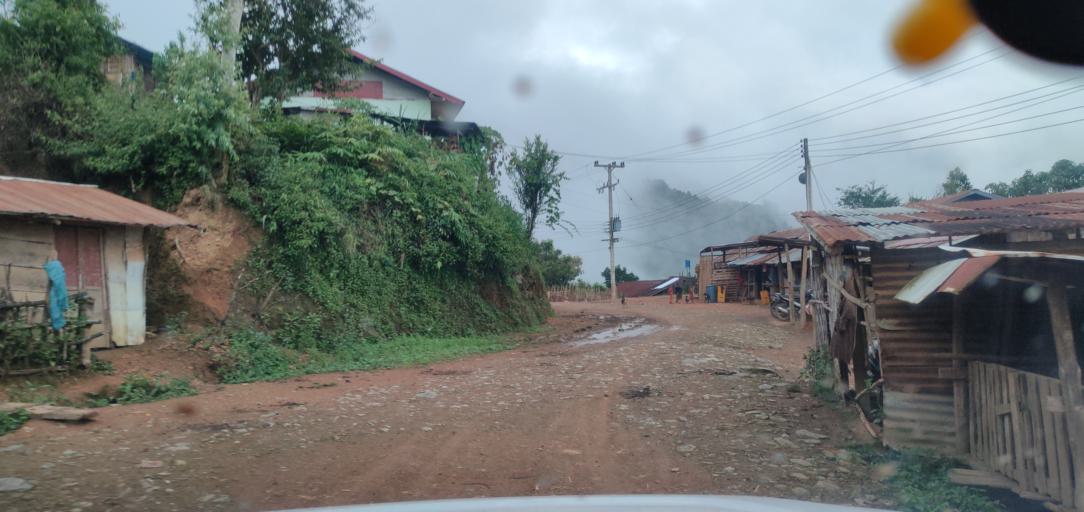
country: LA
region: Phongsali
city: Phongsali
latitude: 21.4413
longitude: 102.2954
